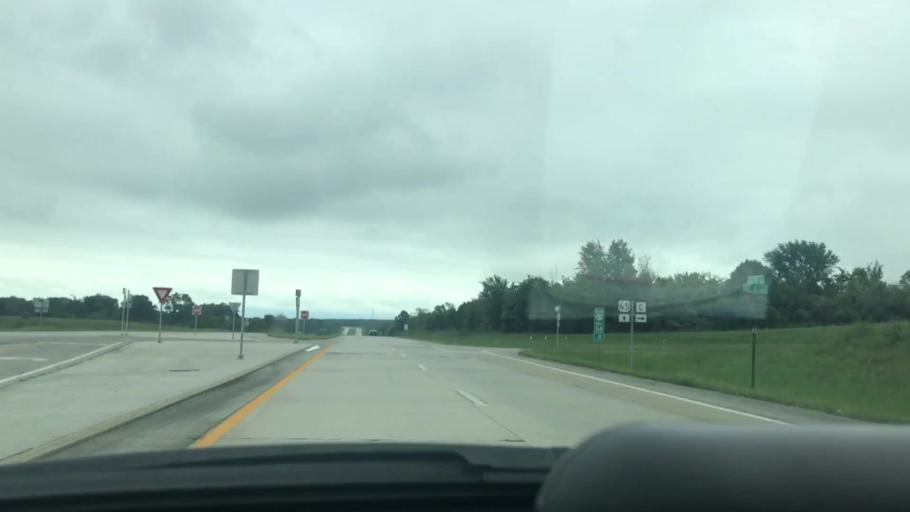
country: US
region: Missouri
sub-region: Greene County
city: Strafford
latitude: 37.3005
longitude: -93.1770
